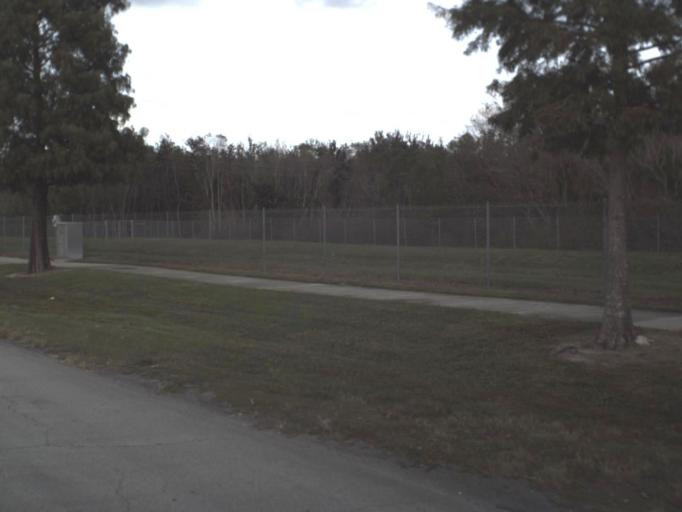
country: US
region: Florida
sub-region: Orange County
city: Oak Ridge
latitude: 28.4937
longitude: -81.4173
